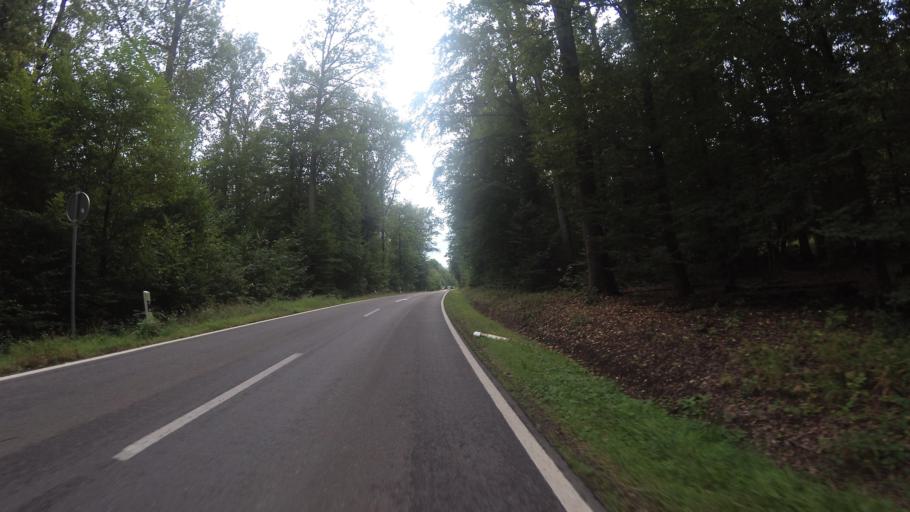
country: DE
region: Saarland
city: Saarbrucken
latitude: 49.2826
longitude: 6.9867
